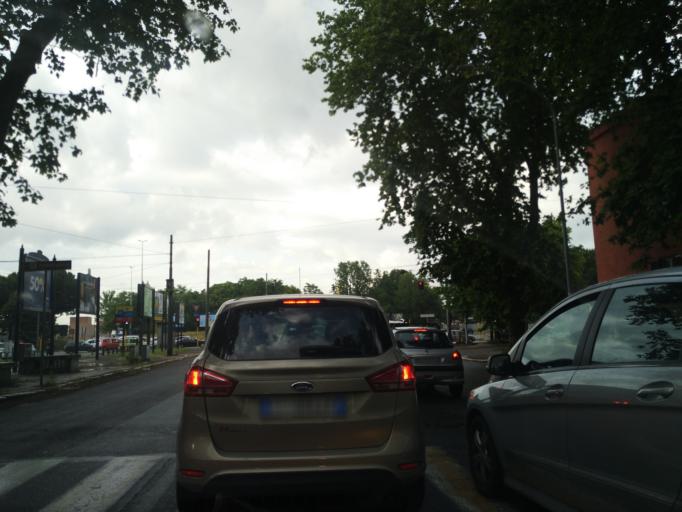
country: IT
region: Latium
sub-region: Citta metropolitana di Roma Capitale
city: Rome
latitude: 41.8942
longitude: 12.5748
